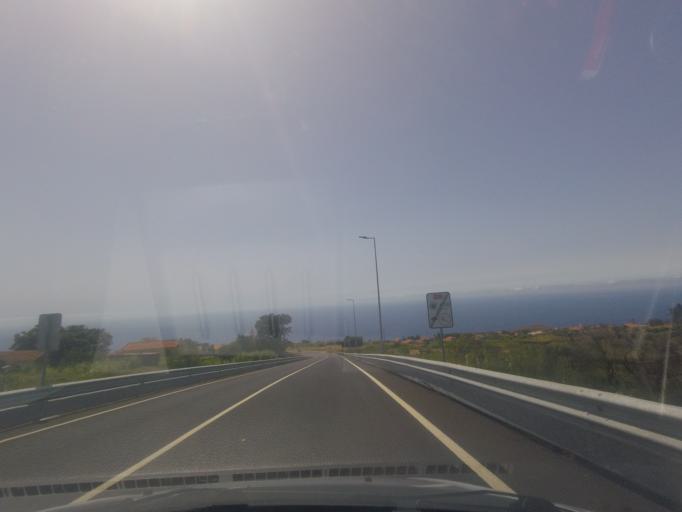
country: PT
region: Madeira
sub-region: Calheta
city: Faja da Ovelha
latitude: 32.8024
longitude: -17.2370
